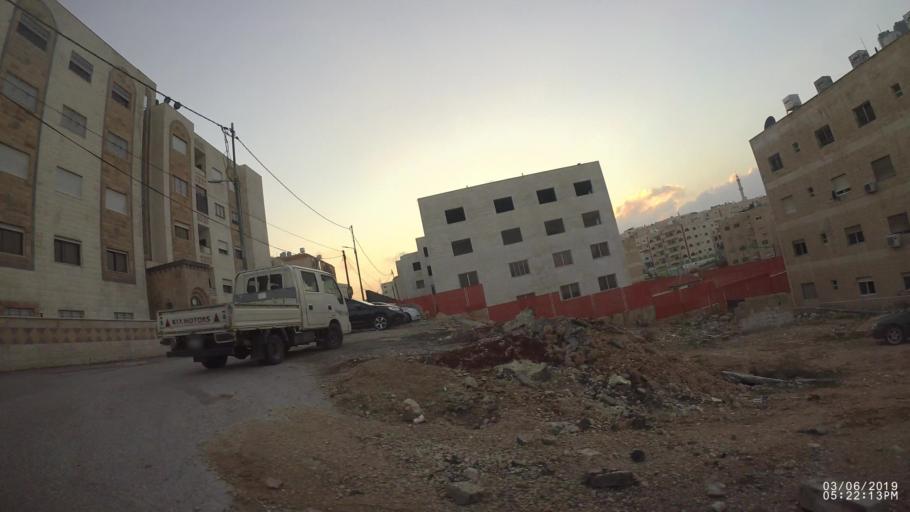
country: JO
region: Amman
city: Amman
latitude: 31.9915
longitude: 35.9564
